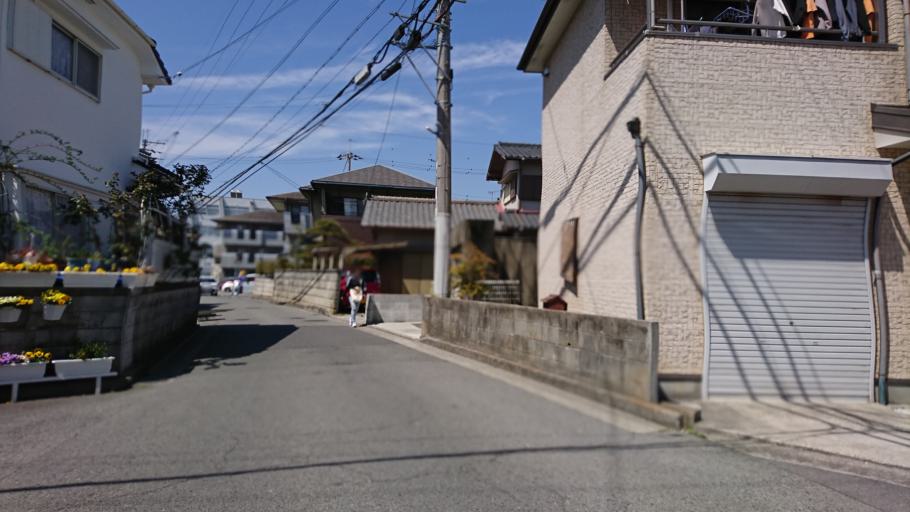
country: JP
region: Hyogo
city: Kakogawacho-honmachi
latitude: 34.7456
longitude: 134.8837
